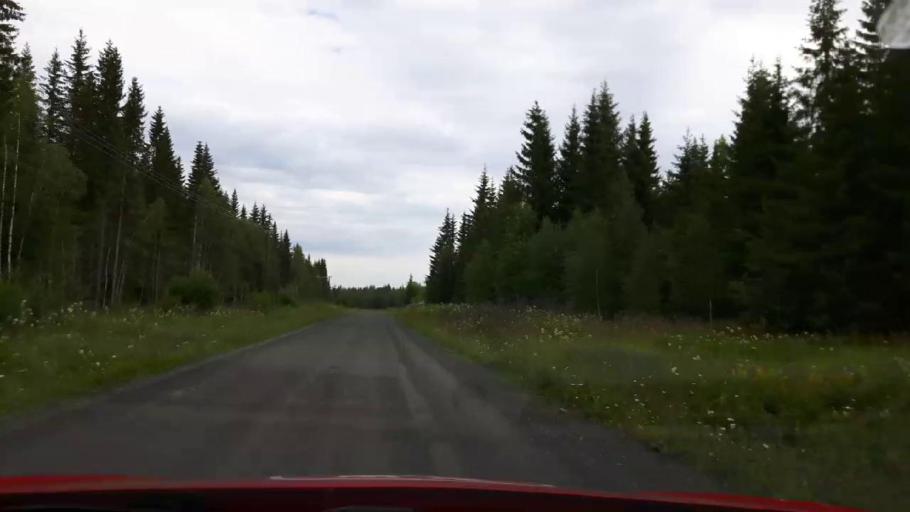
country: SE
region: Jaemtland
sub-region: Stroemsunds Kommun
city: Stroemsund
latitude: 63.4918
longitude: 15.3129
